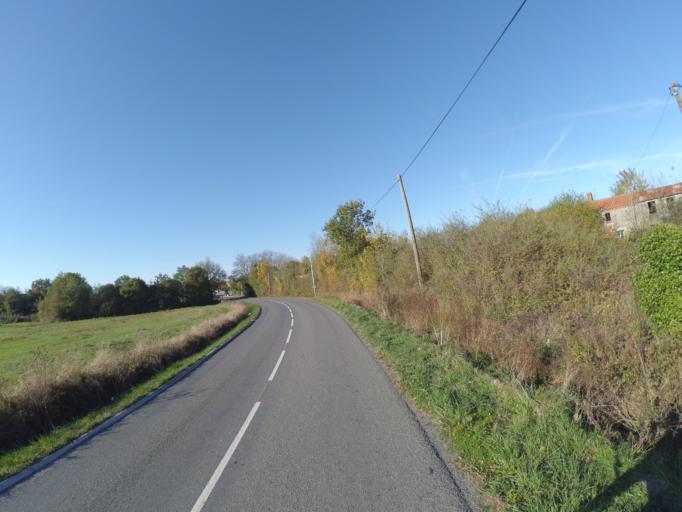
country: FR
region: Pays de la Loire
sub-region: Departement de la Loire-Atlantique
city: Saint-Lumine-de-Clisson
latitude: 47.0811
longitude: -1.3318
